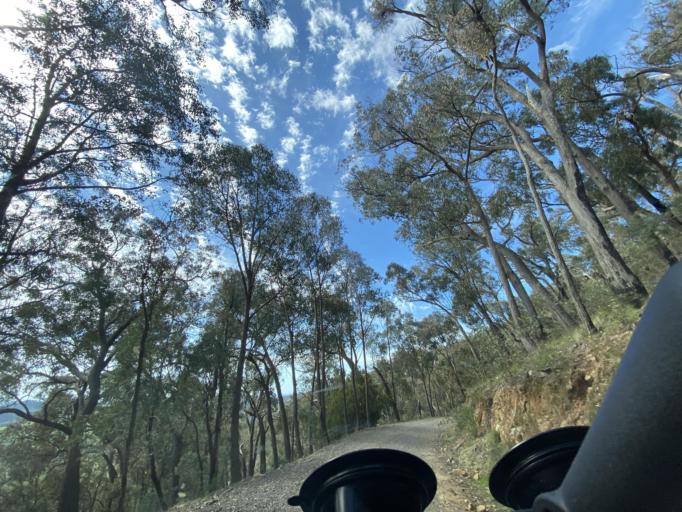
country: AU
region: Victoria
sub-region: Mansfield
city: Mansfield
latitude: -36.8108
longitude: 146.1022
